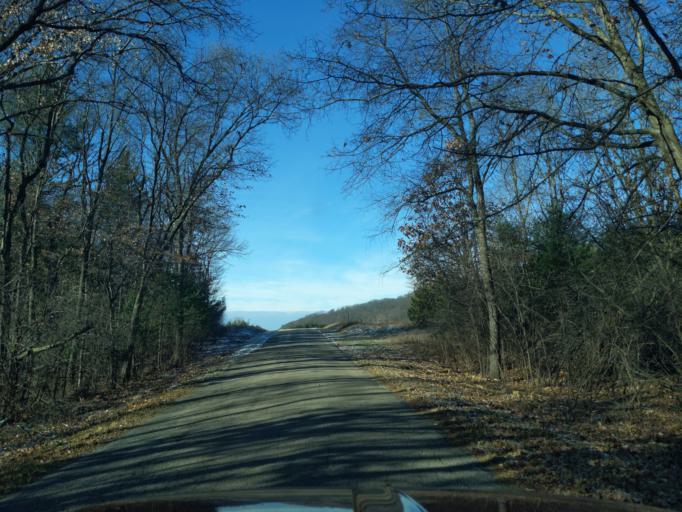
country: US
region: Wisconsin
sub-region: Waushara County
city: Silver Lake
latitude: 44.1128
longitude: -89.1732
